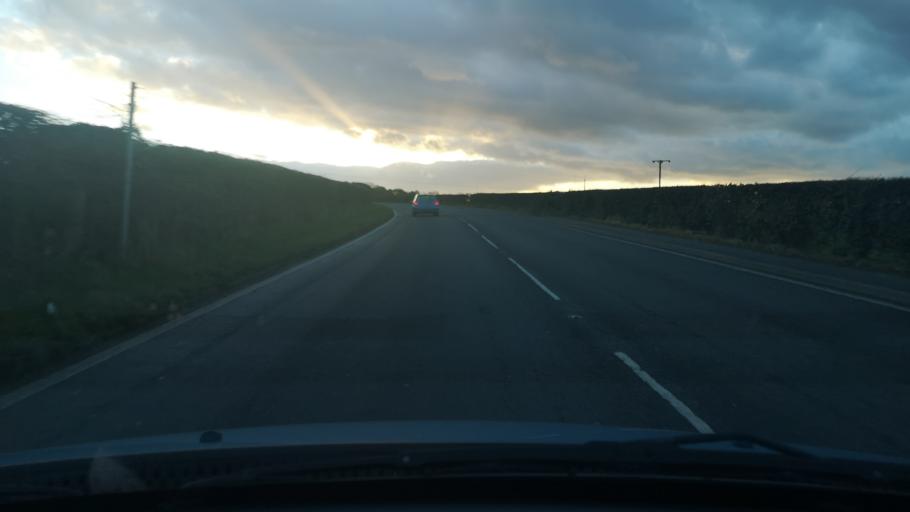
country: GB
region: England
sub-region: City and Borough of Wakefield
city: Middlestown
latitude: 53.6276
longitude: -1.5725
